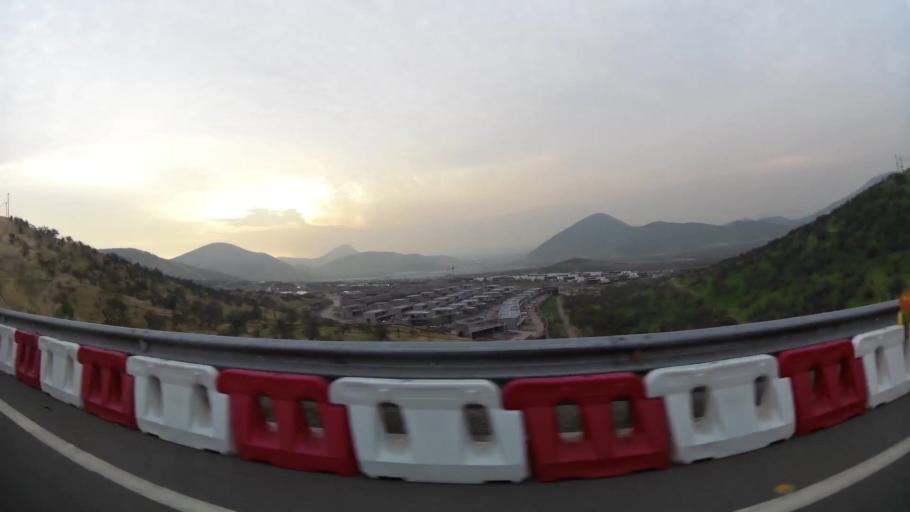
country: CL
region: Santiago Metropolitan
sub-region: Provincia de Chacabuco
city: Chicureo Abajo
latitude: -33.3277
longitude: -70.6253
